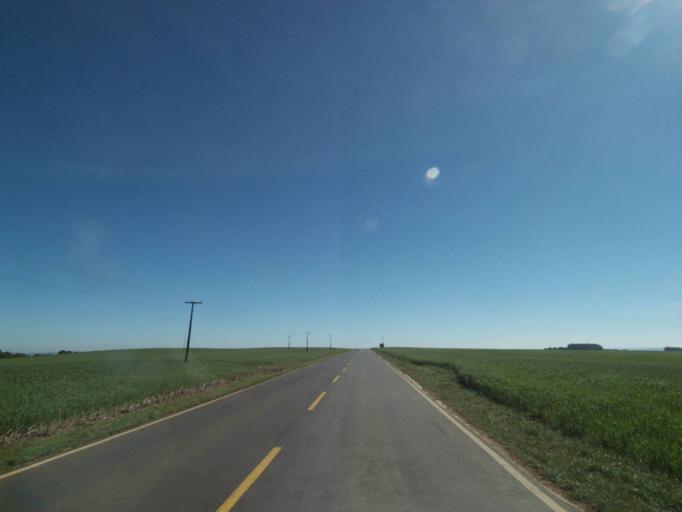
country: BR
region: Parana
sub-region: Tibagi
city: Tibagi
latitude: -24.5701
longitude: -50.2819
